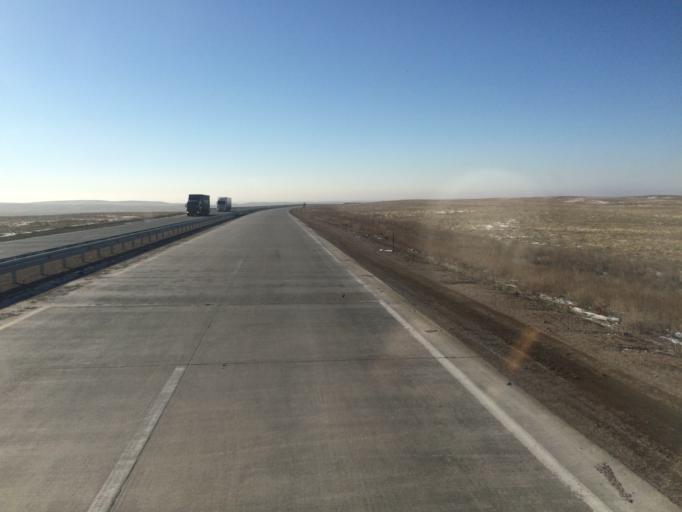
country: KZ
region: Zhambyl
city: Georgiyevka
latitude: 43.3423
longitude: 74.4901
